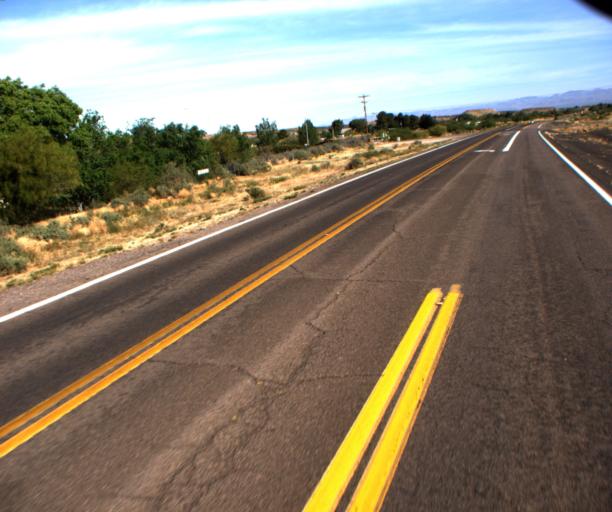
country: US
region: Arizona
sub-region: Graham County
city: Swift Trail Junction
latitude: 32.6853
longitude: -109.7073
